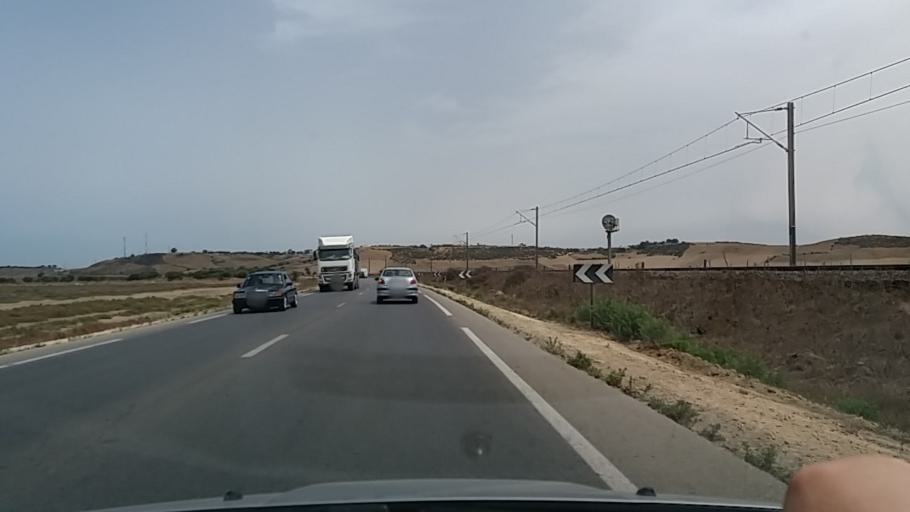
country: MA
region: Tanger-Tetouan
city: Asilah
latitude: 35.5047
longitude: -6.0035
